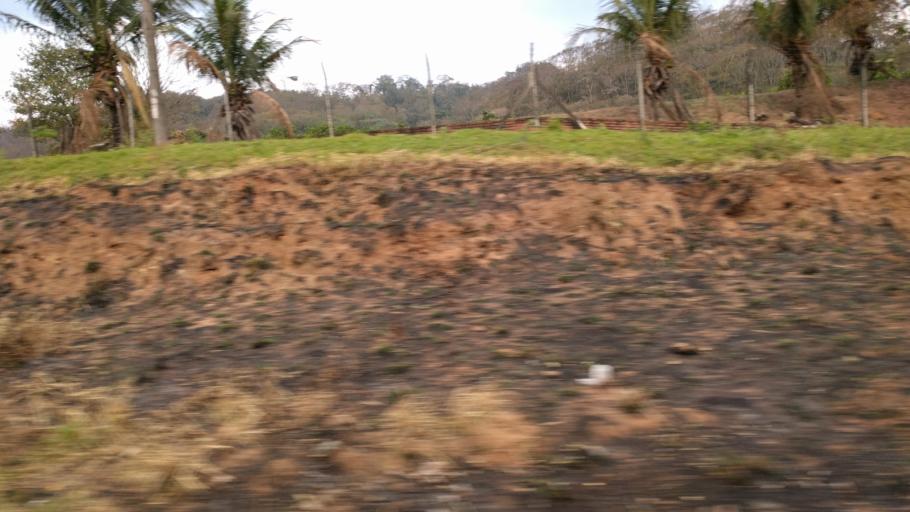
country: BO
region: Santa Cruz
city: Jorochito
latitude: -18.0813
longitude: -63.4487
